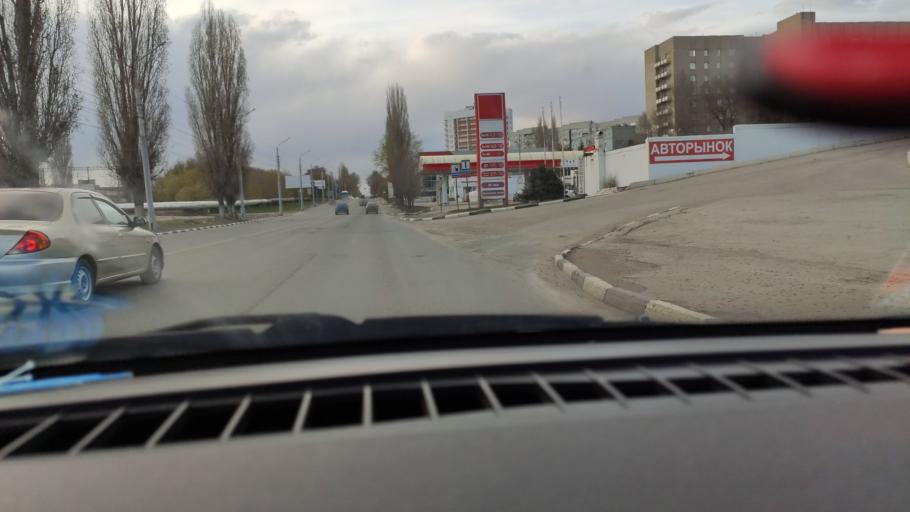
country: RU
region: Saratov
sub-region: Saratovskiy Rayon
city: Saratov
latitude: 51.5715
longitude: 45.9937
